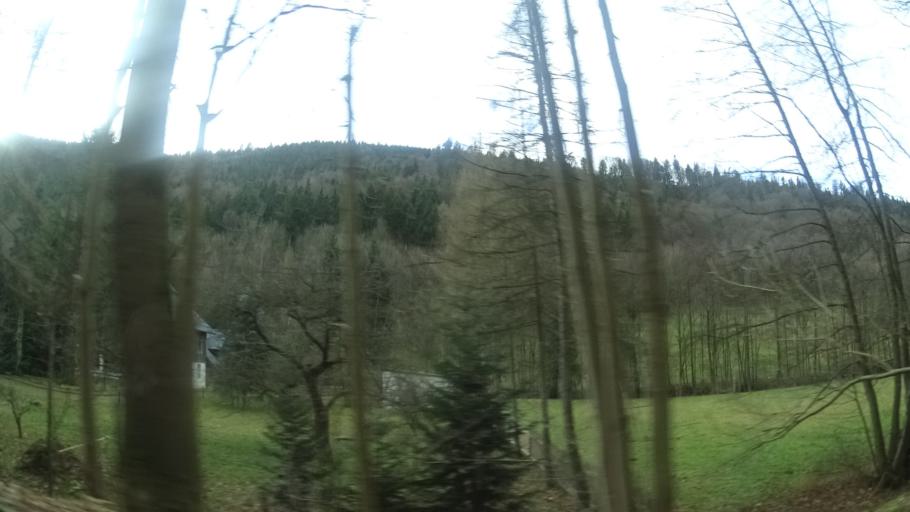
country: DE
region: Thuringia
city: Sitzendorf
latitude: 50.6259
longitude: 11.1858
